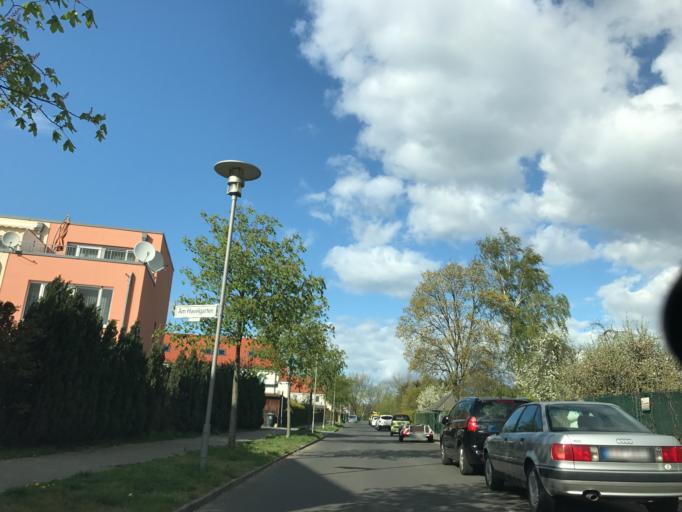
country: DE
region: Berlin
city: Haselhorst
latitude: 52.5551
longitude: 13.2298
